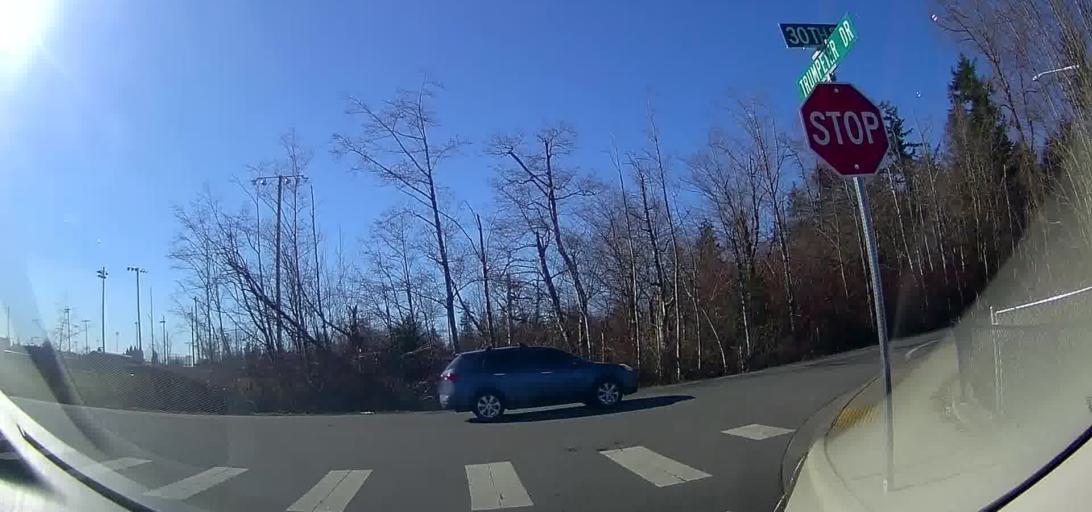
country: US
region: Washington
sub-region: Skagit County
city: Mount Vernon
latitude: 48.4414
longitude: -122.3022
